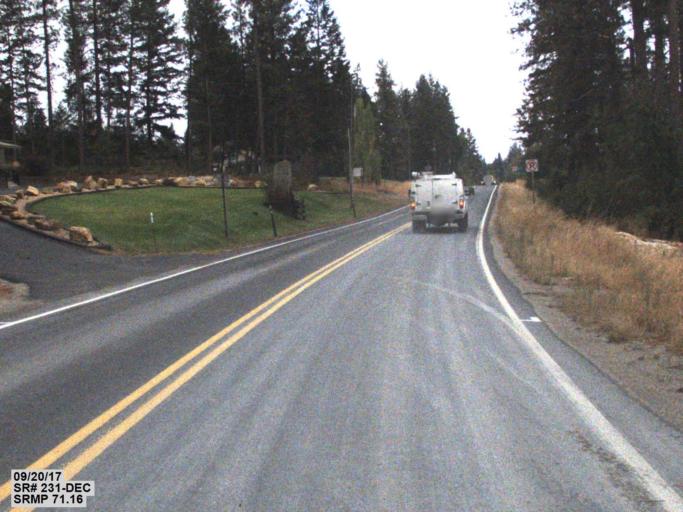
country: US
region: Washington
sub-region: Stevens County
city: Chewelah
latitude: 48.1665
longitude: -117.7226
